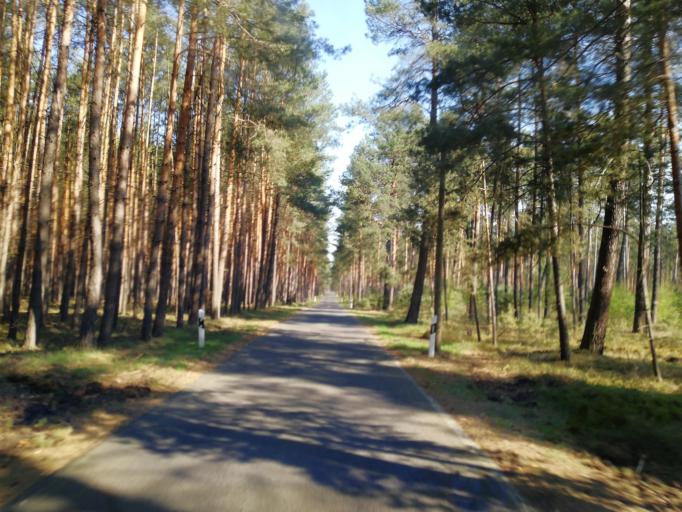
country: DE
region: Brandenburg
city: Bronkow
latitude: 51.6743
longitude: 13.8640
